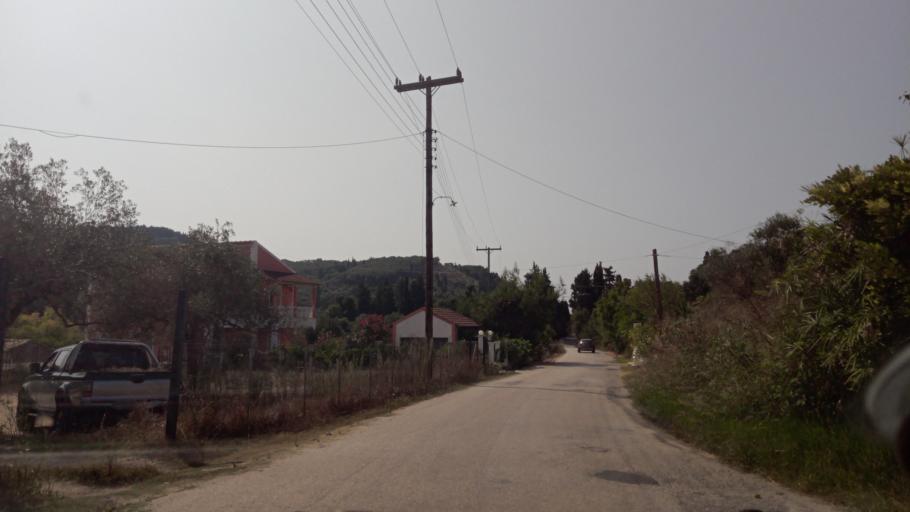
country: GR
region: Ionian Islands
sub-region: Nomos Kerkyras
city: Perivoli
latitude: 39.4034
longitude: 20.0268
